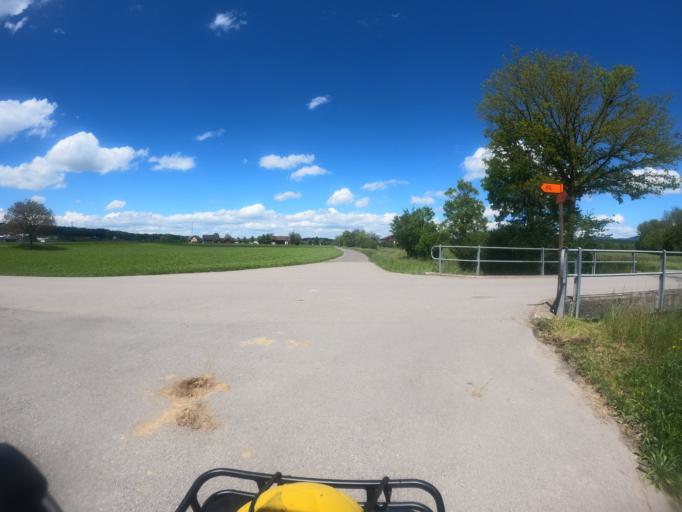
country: CH
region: Aargau
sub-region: Bezirk Muri
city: Merenschwand
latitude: 47.2313
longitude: 8.3957
